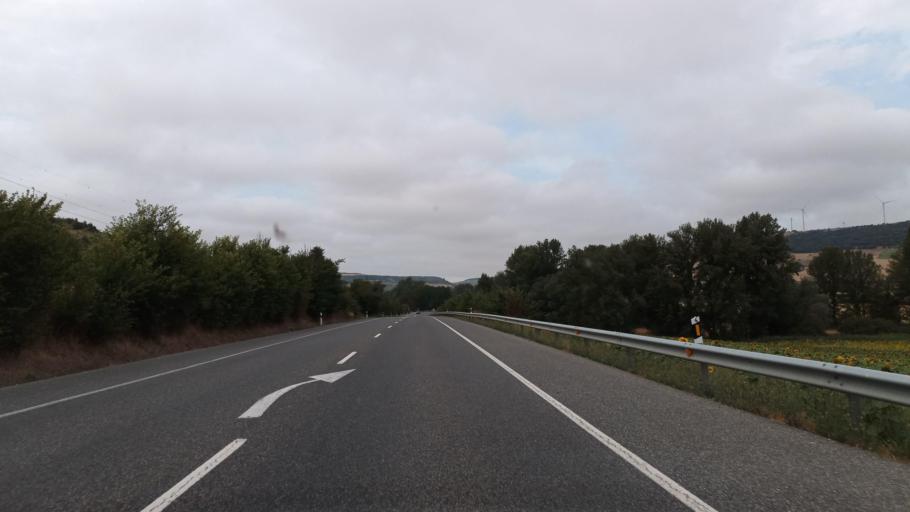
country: ES
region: Castille and Leon
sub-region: Provincia de Burgos
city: Santa Olalla de Bureba
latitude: 42.4678
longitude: -3.4336
